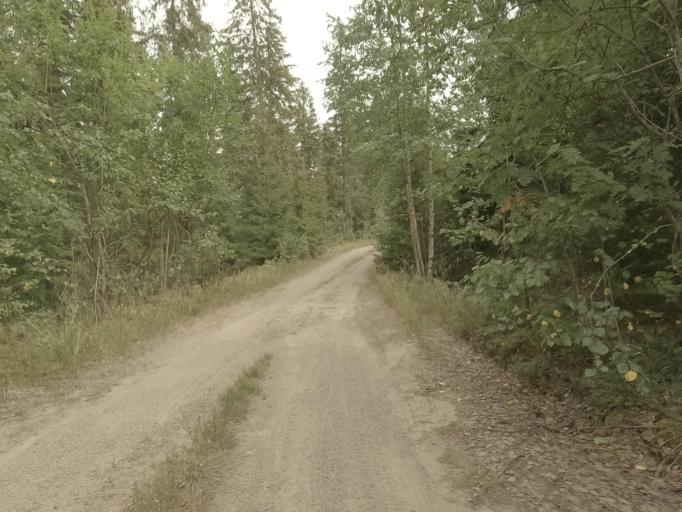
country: RU
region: Leningrad
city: Kamennogorsk
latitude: 61.0177
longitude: 29.2020
